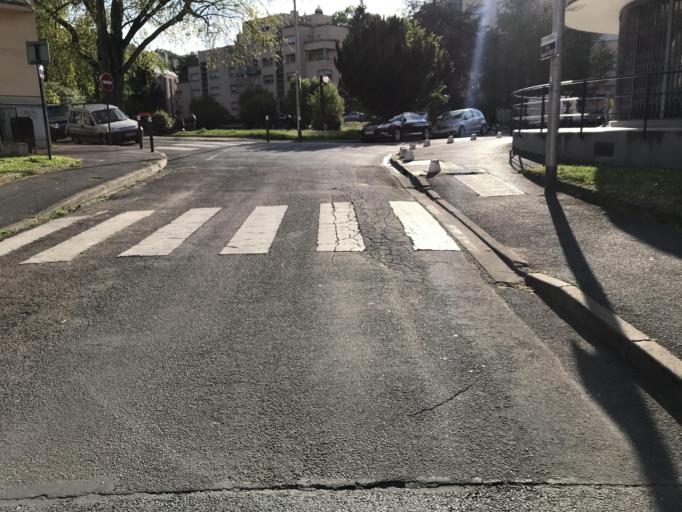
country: FR
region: Ile-de-France
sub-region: Departement des Hauts-de-Seine
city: Chatenay-Malabry
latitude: 48.7636
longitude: 2.2600
